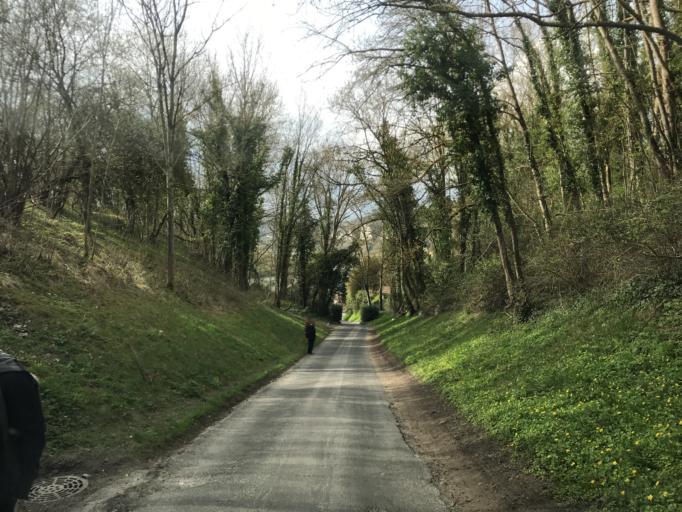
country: FR
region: Haute-Normandie
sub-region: Departement de l'Eure
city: Les Andelys
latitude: 49.2392
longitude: 1.4032
